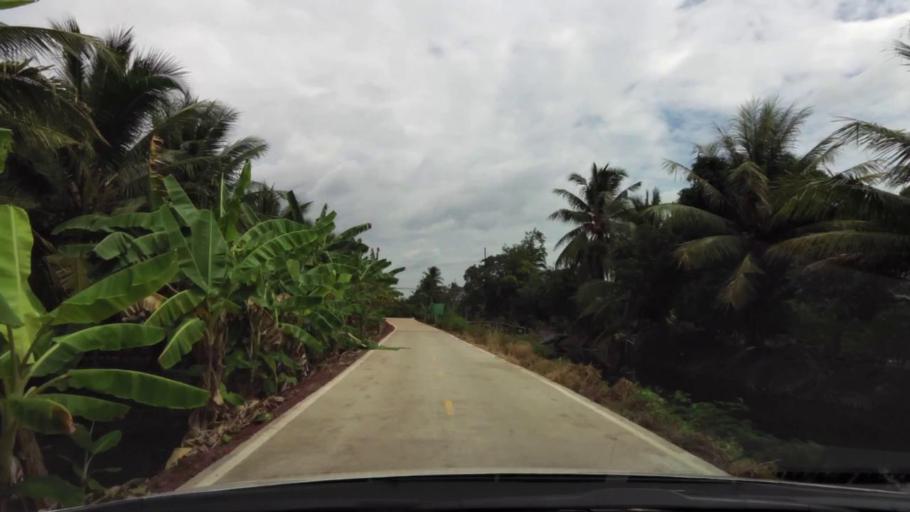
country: TH
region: Ratchaburi
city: Damnoen Saduak
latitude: 13.5558
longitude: 99.9805
